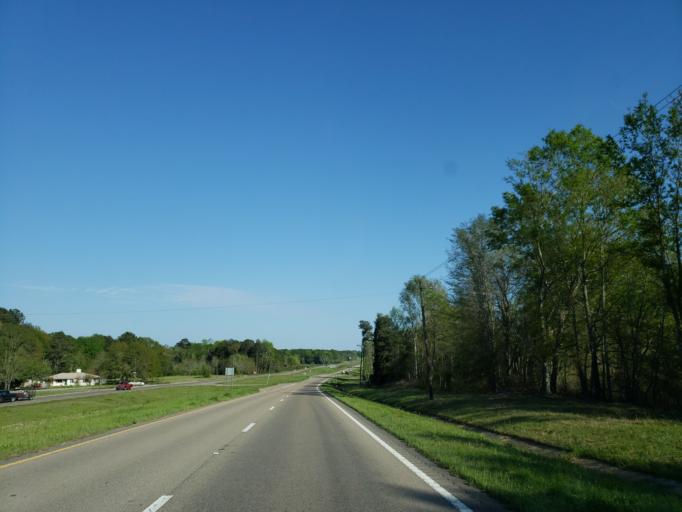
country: US
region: Mississippi
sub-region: Jones County
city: Ellisville
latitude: 31.6852
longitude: -89.3179
